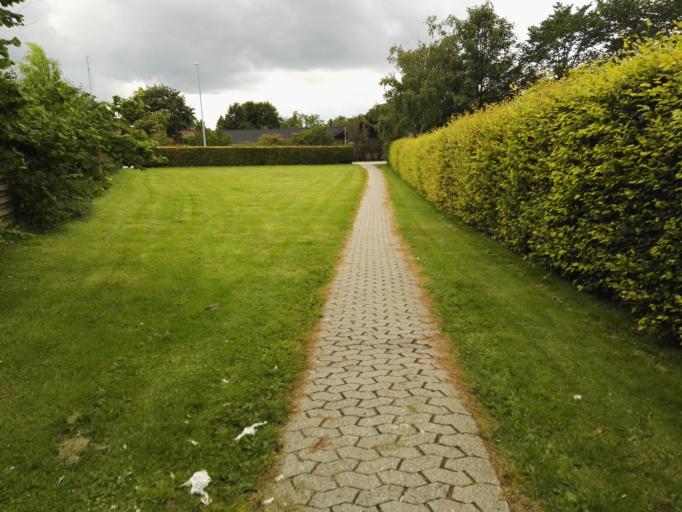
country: DK
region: Capital Region
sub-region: Egedal Kommune
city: Stenlose
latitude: 55.7666
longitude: 12.1863
